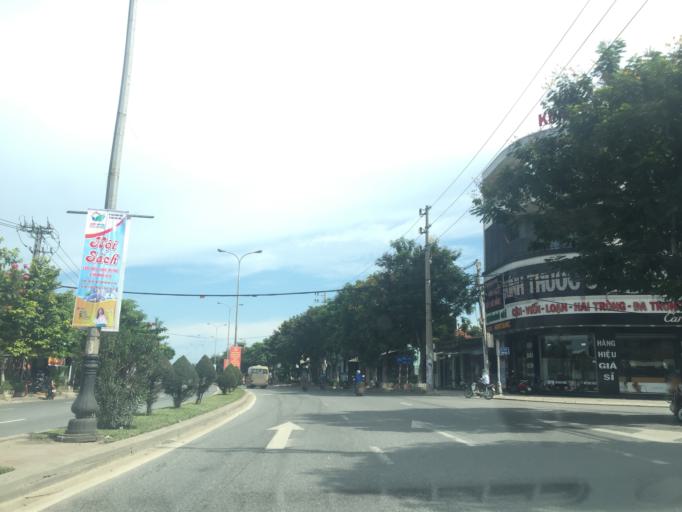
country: VN
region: Da Nang
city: Lien Chieu
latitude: 16.0673
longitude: 108.1525
